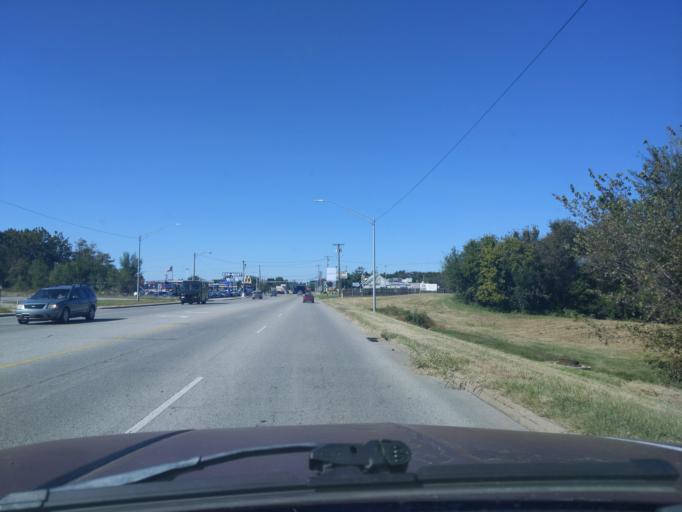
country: US
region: Oklahoma
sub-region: Creek County
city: Sapulpa
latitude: 35.9885
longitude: -96.1105
